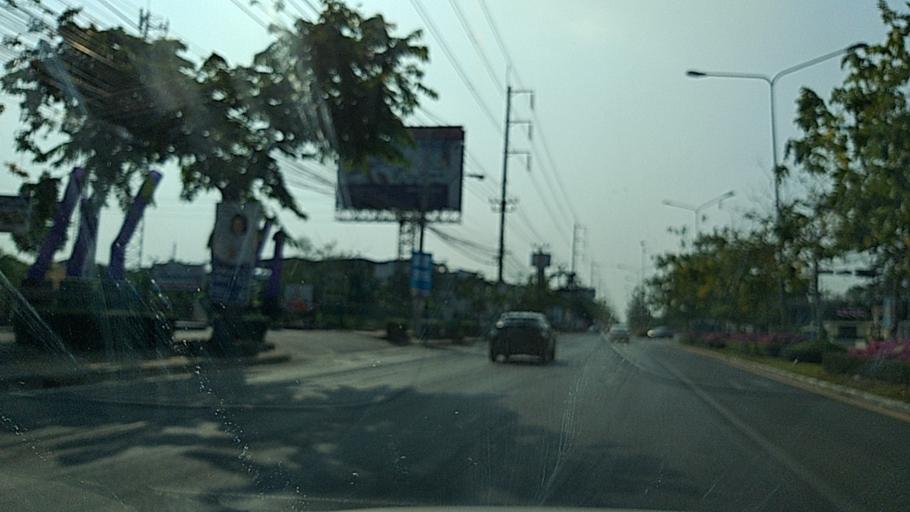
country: TH
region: Bangkok
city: Don Mueang
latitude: 13.9300
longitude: 100.5767
